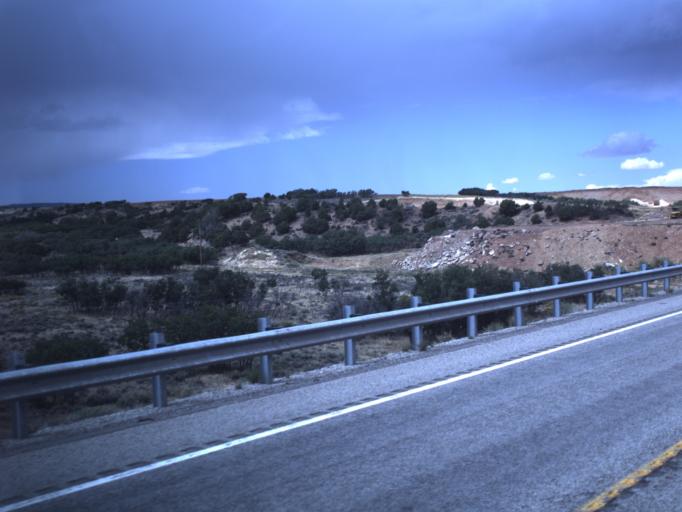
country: US
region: Utah
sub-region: San Juan County
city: Monticello
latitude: 37.8279
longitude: -109.3369
